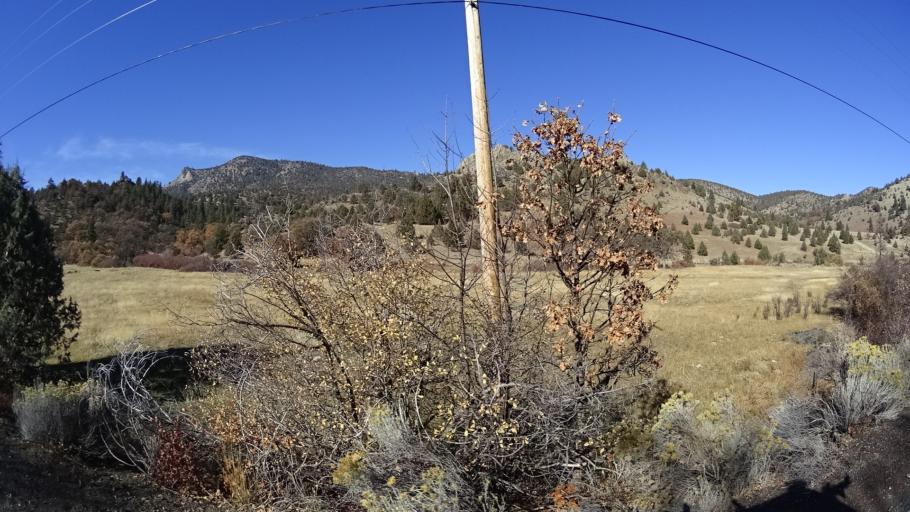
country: US
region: California
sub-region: Siskiyou County
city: Weed
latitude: 41.4710
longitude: -122.5900
